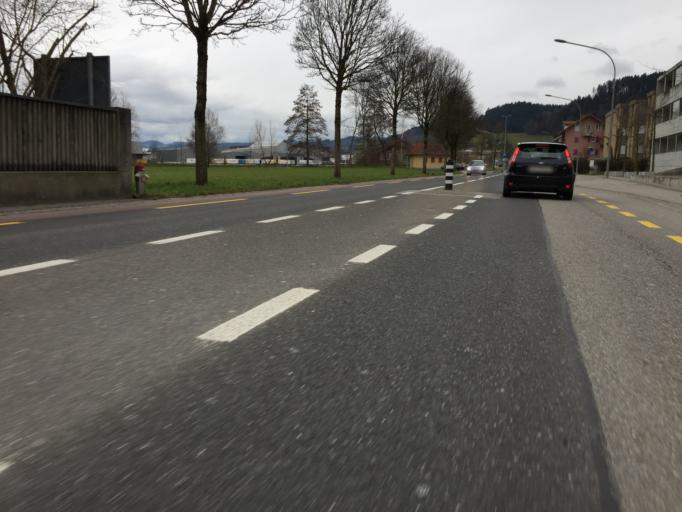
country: CH
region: Bern
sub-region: Emmental District
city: Oberburg
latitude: 47.0455
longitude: 7.6225
